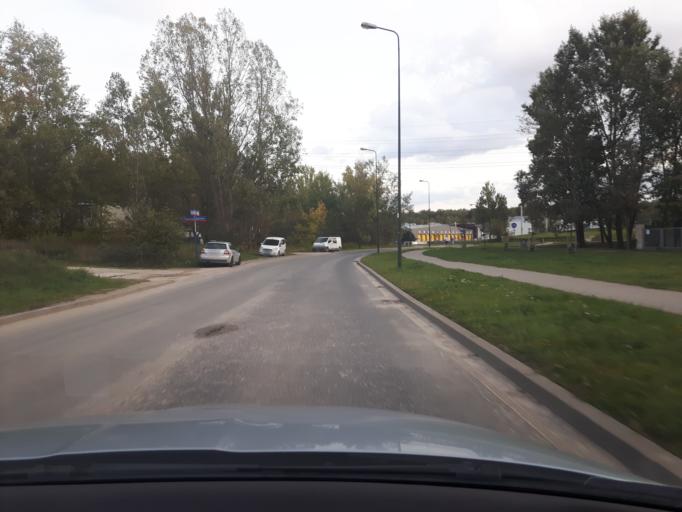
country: PL
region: Masovian Voivodeship
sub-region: Warszawa
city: Kabaty
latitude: 52.1280
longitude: 21.0689
